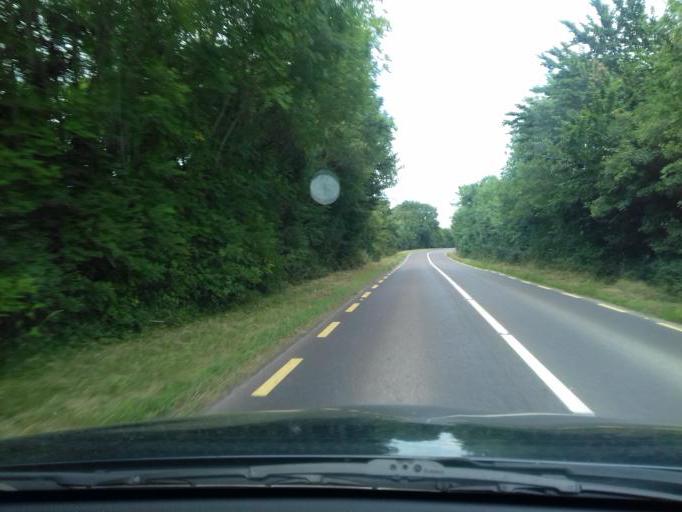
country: IE
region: Leinster
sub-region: Wicklow
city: Baltinglass
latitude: 52.9563
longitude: -6.7059
